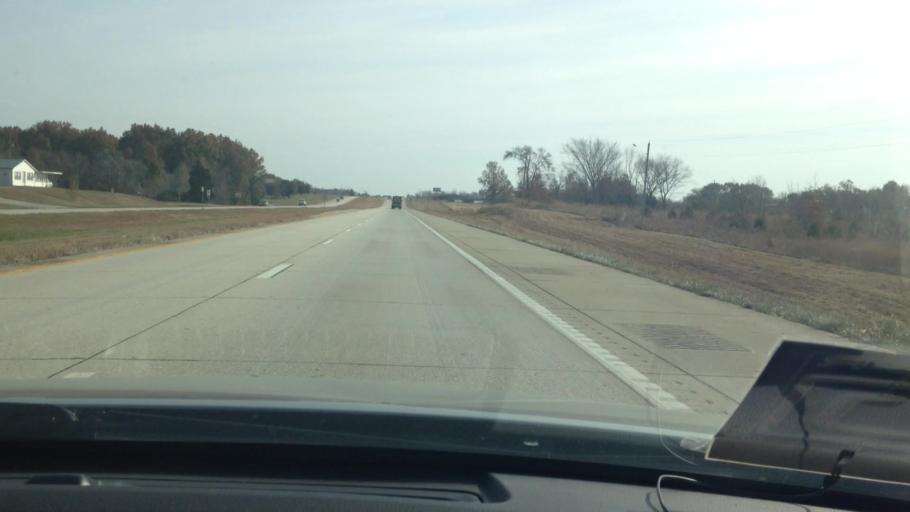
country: US
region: Missouri
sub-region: Henry County
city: Clinton
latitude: 38.4183
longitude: -93.8665
